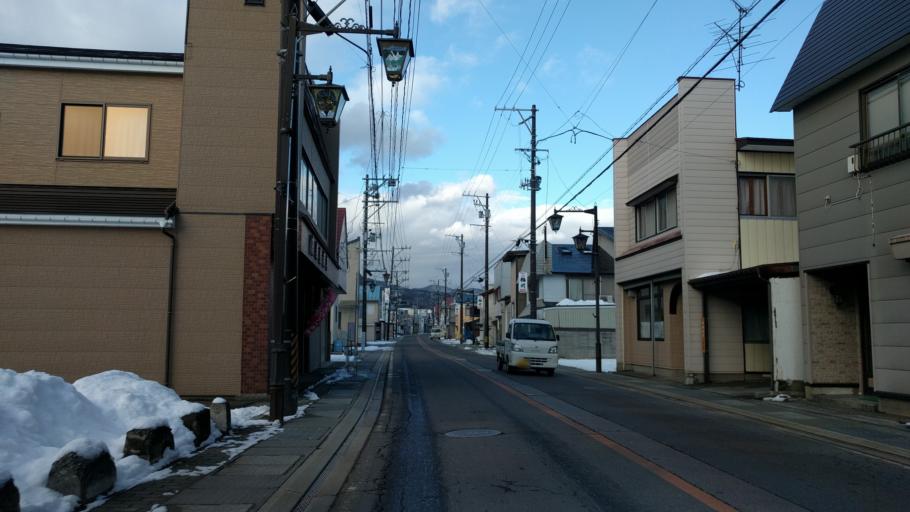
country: JP
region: Fukushima
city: Inawashiro
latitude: 37.5573
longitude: 140.1066
